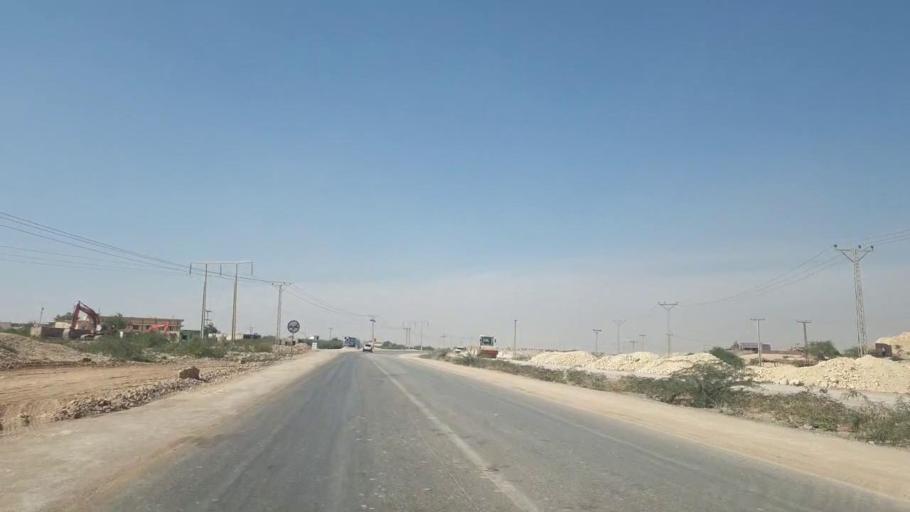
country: PK
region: Sindh
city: Hala
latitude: 25.7353
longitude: 68.2907
